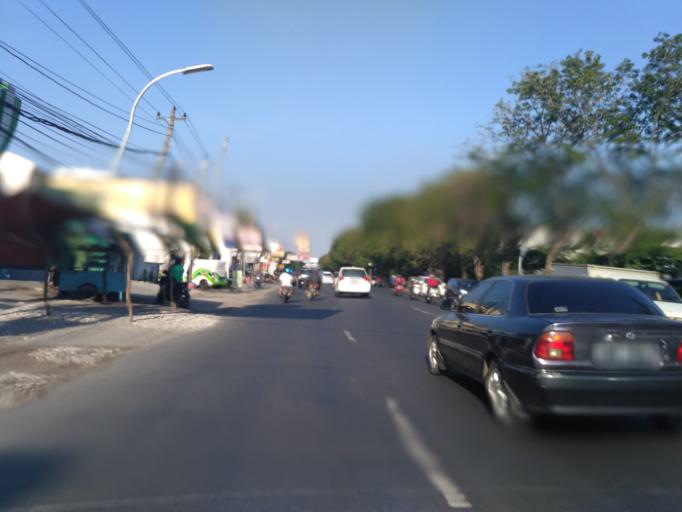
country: ID
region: Central Java
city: Semarang
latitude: -7.0080
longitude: 110.4622
